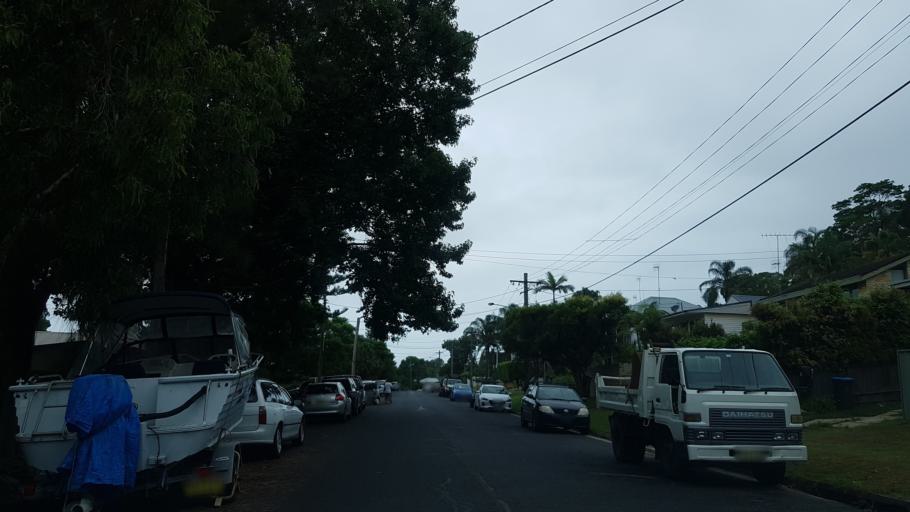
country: AU
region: New South Wales
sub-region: Pittwater
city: North Narrabeen
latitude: -33.7061
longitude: 151.2896
